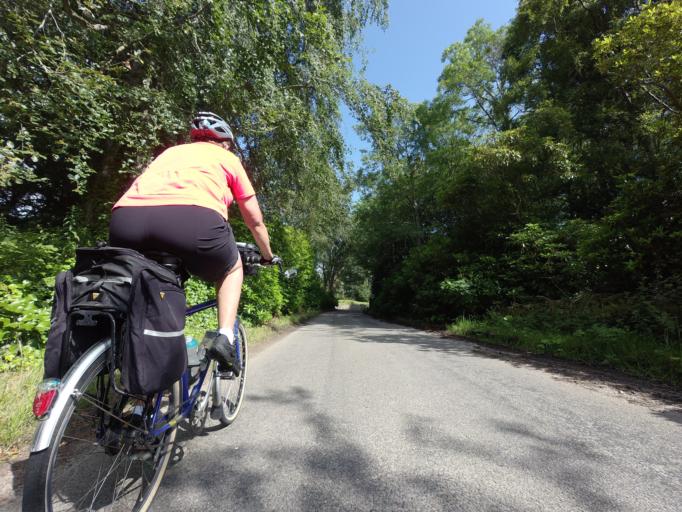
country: GB
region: Scotland
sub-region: Highland
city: Alness
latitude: 57.7162
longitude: -4.2173
